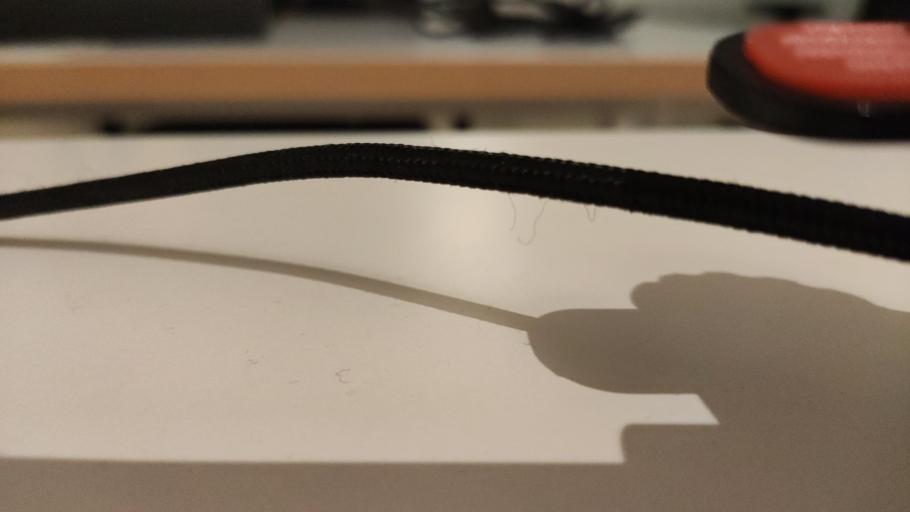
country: RU
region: Moskovskaya
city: Shaburnovo
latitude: 56.4329
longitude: 37.9329
